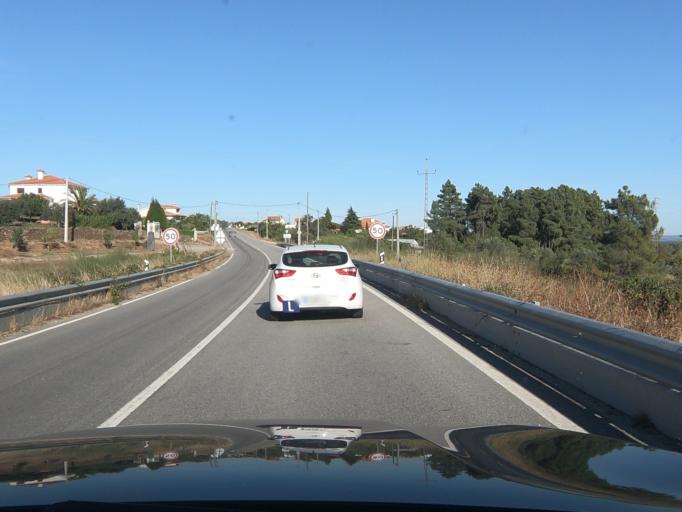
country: PT
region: Vila Real
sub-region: Sabrosa
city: Sabrosa
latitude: 41.2614
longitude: -7.6023
